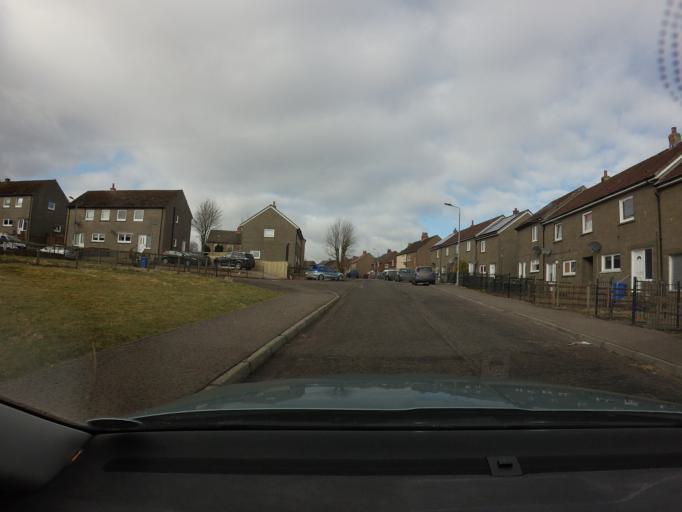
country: GB
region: Scotland
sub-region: South Lanarkshire
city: Lanark
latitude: 55.5973
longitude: -3.7768
